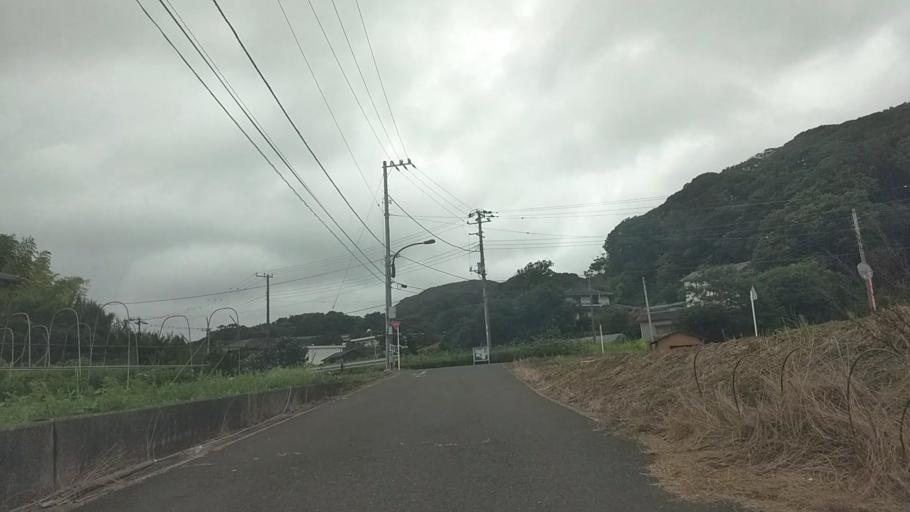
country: JP
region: Kanagawa
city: Hayama
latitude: 35.2322
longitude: 139.6236
